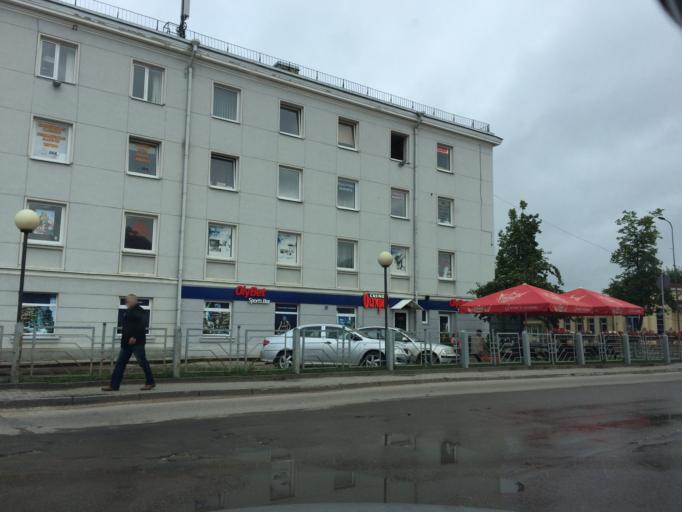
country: LV
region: Rezekne
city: Rezekne
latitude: 56.4993
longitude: 27.3300
